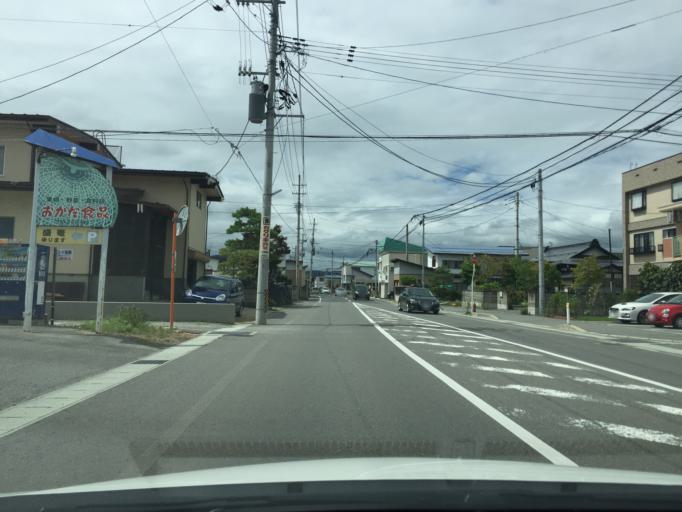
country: JP
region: Yamagata
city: Yonezawa
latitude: 37.9025
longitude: 140.1156
